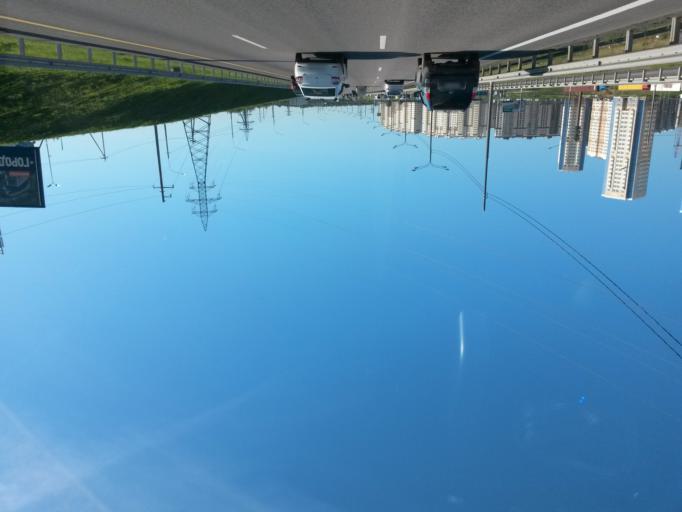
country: RU
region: Moskovskaya
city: Vostryakovo
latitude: 55.3905
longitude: 37.7761
